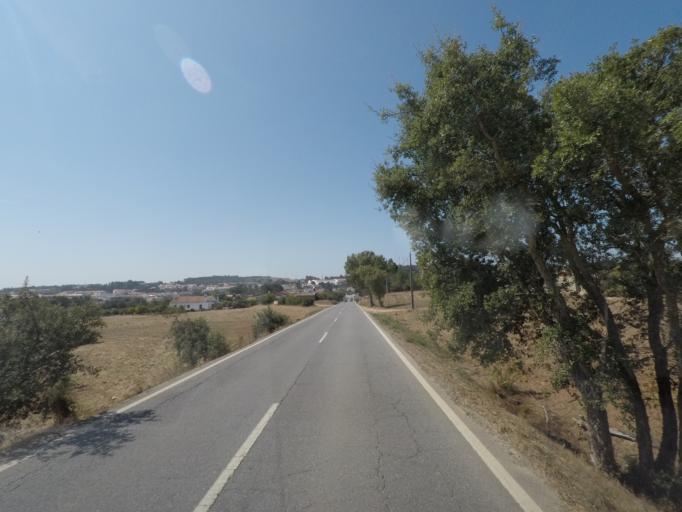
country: PT
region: Beja
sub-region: Odemira
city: Sao Teotonio
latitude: 37.5193
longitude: -8.7052
